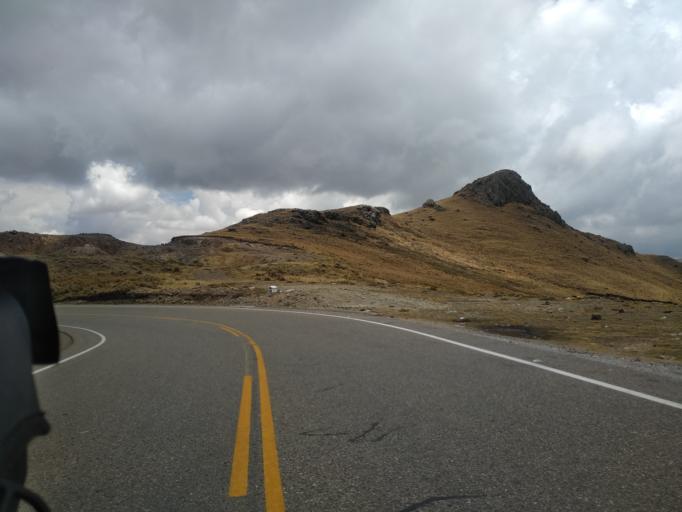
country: PE
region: La Libertad
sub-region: Provincia de Santiago de Chuco
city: Quiruvilca
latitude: -7.9711
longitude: -78.2070
